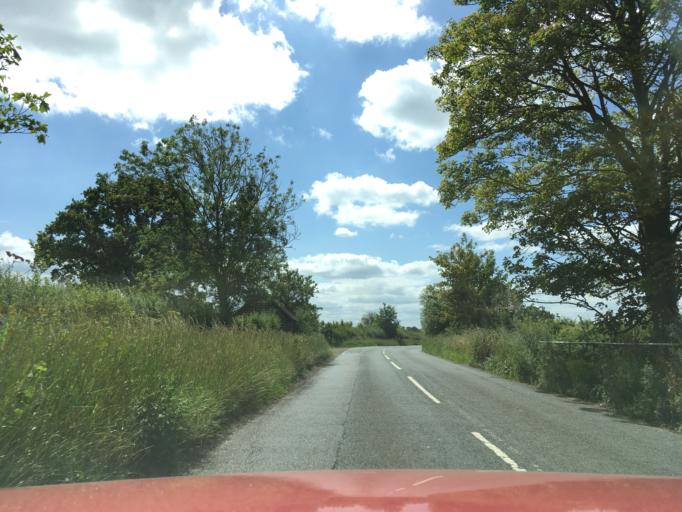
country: GB
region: England
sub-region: Buckinghamshire
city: Winslow
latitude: 51.9302
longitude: -0.8352
